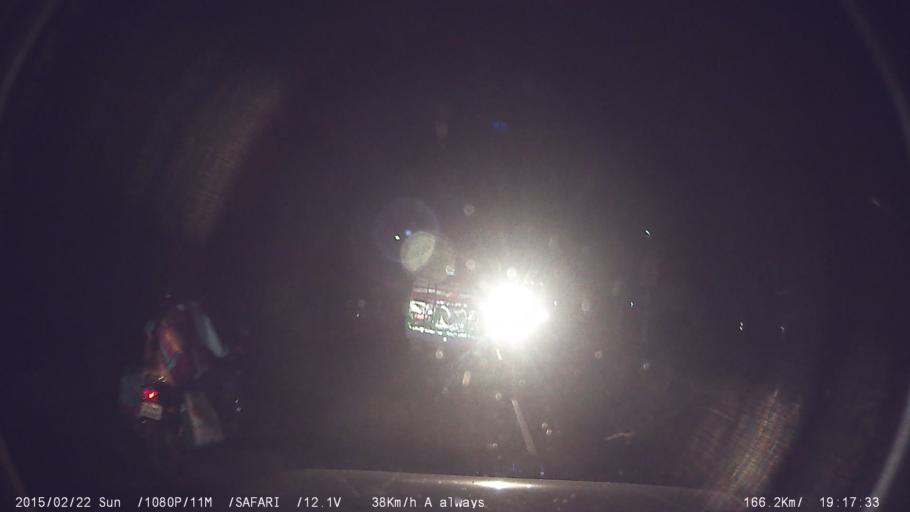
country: IN
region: Tamil Nadu
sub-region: Theni
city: Periyakulam
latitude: 10.0994
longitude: 77.5350
